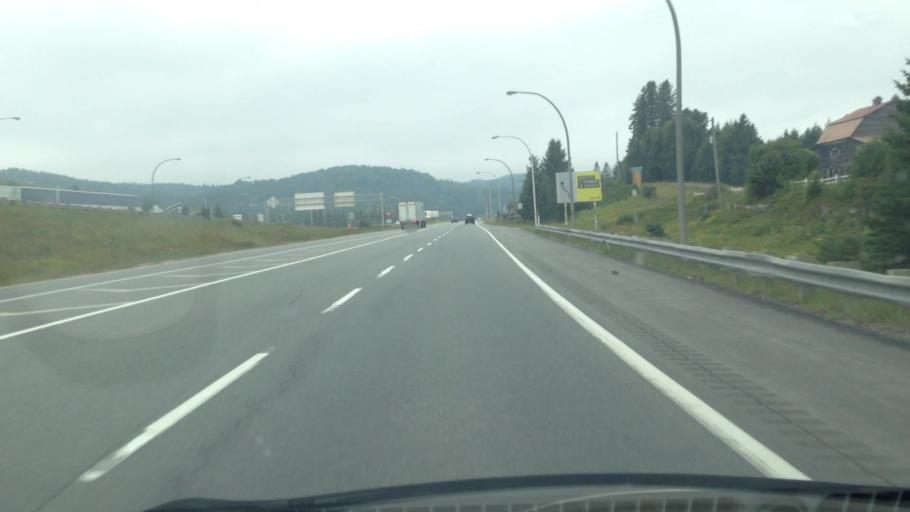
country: CA
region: Quebec
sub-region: Laurentides
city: Sainte-Agathe-des-Monts
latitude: 46.0629
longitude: -74.2953
